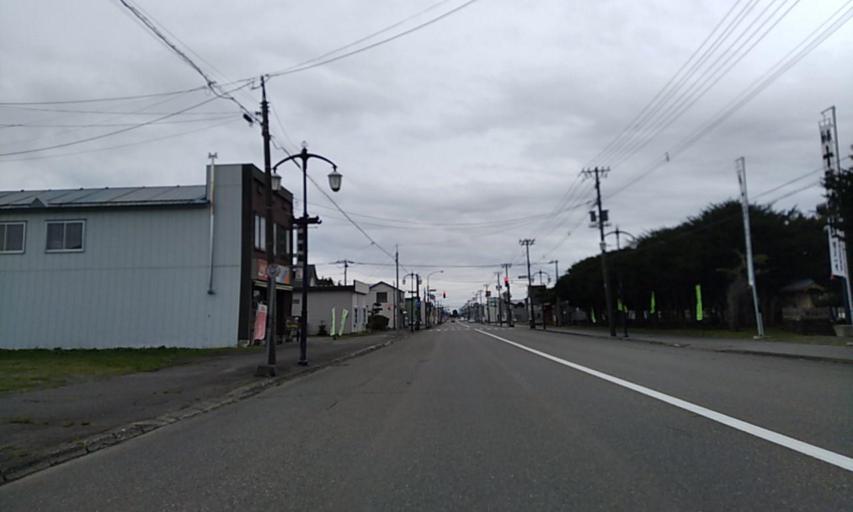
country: JP
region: Hokkaido
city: Obihiro
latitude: 42.2922
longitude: 143.3127
